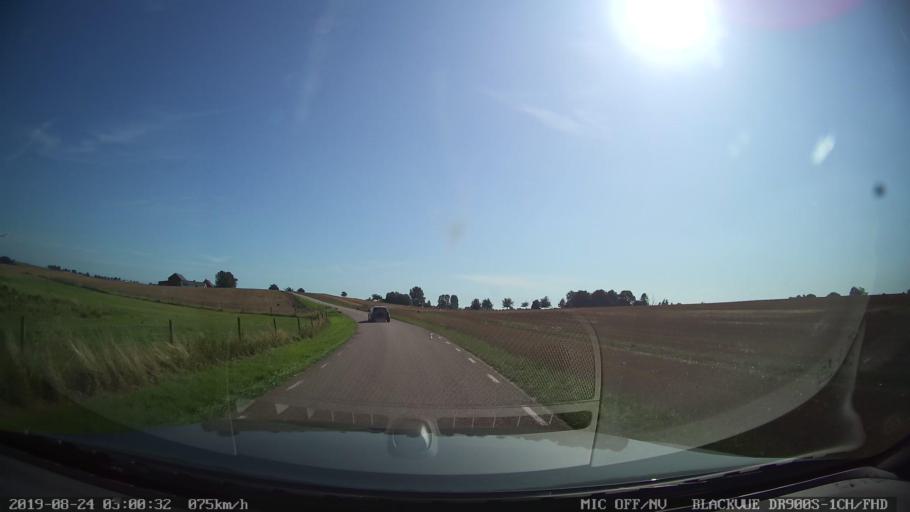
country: SE
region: Skane
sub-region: Skurups Kommun
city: Skurup
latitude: 55.4554
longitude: 13.4287
